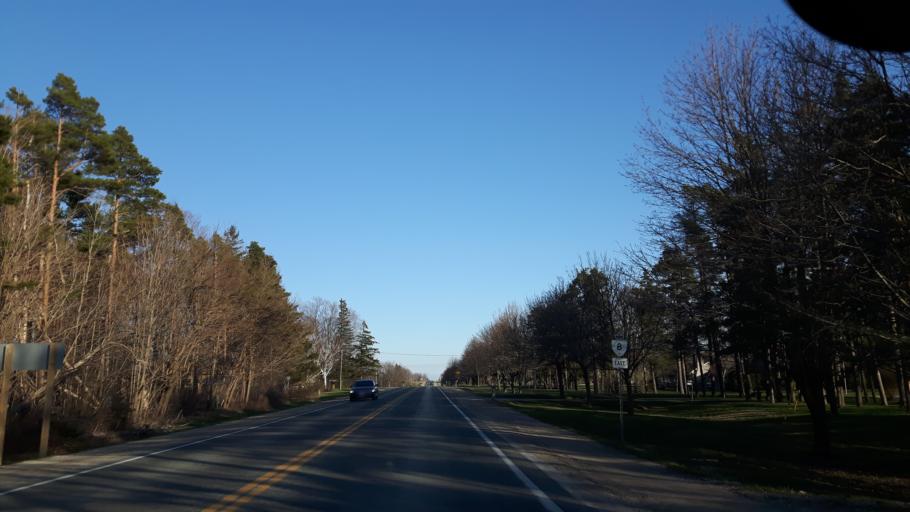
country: CA
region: Ontario
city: Goderich
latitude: 43.7273
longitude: -81.6851
